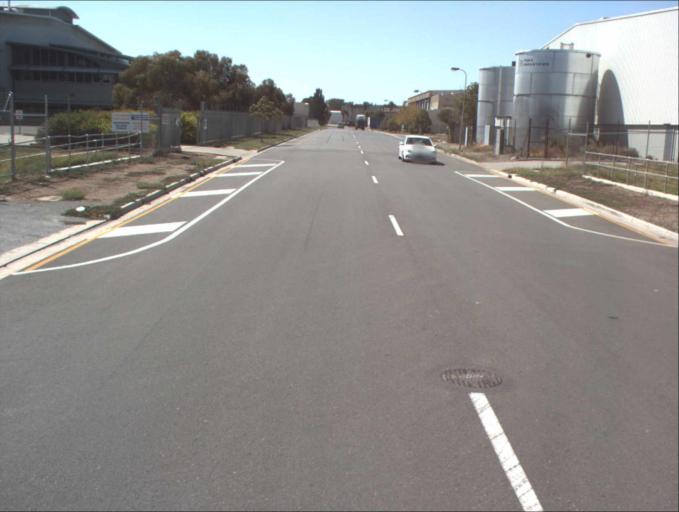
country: AU
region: South Australia
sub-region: Charles Sturt
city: Woodville North
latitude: -34.8434
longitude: 138.5596
